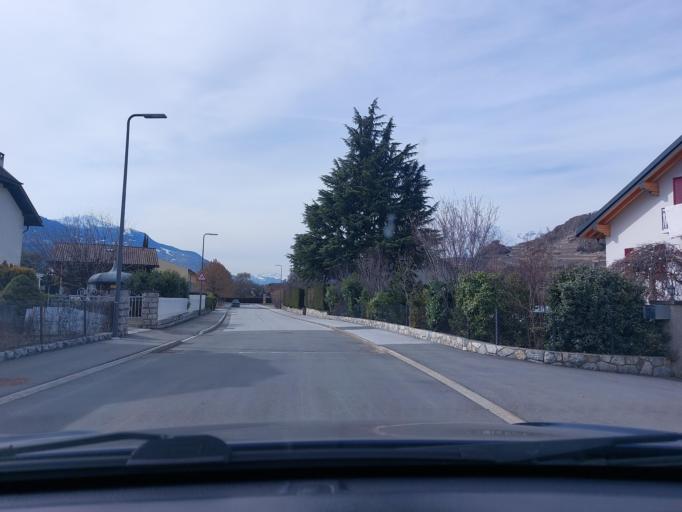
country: CH
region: Valais
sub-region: Sion District
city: Saint-Leonard
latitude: 46.2518
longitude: 7.4126
